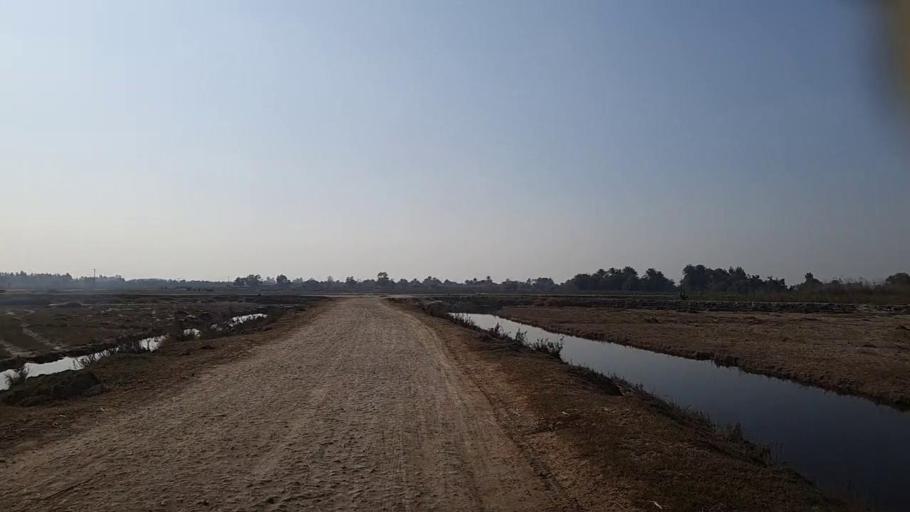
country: PK
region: Sindh
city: Mirpur Mathelo
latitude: 27.8916
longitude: 69.6059
